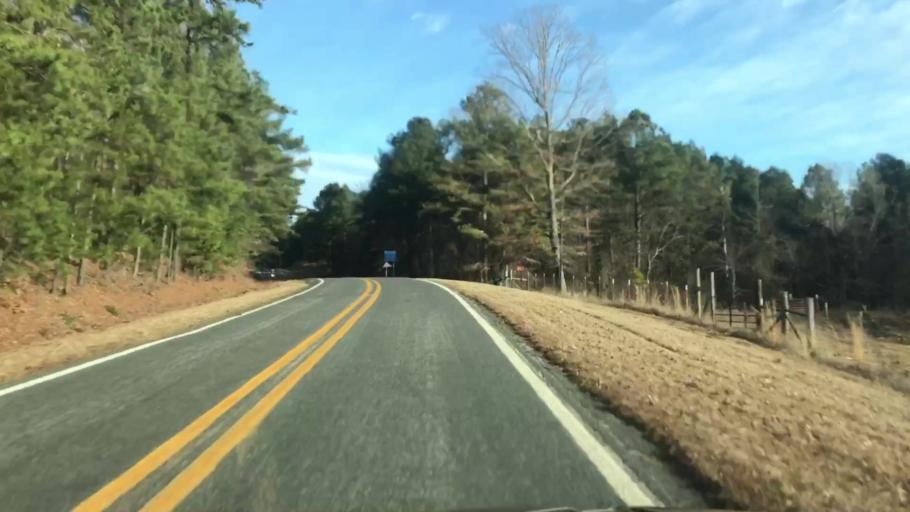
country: US
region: Arkansas
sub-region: Garland County
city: Rockwell
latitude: 34.4822
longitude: -93.2733
